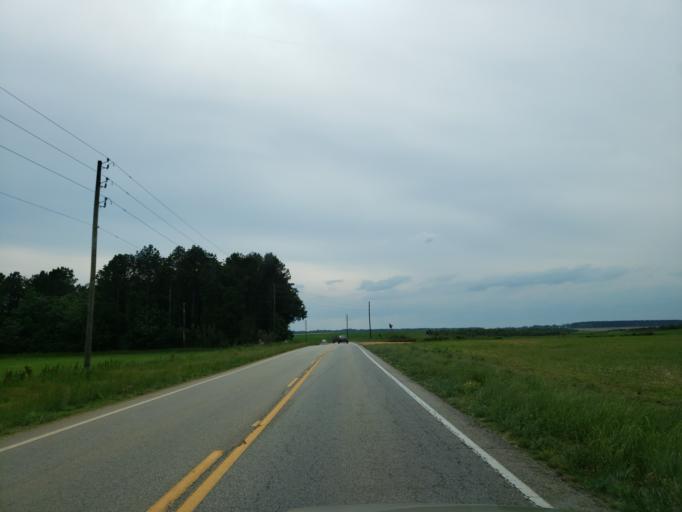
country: US
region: Georgia
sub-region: Macon County
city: Marshallville
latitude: 32.3665
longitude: -83.9133
